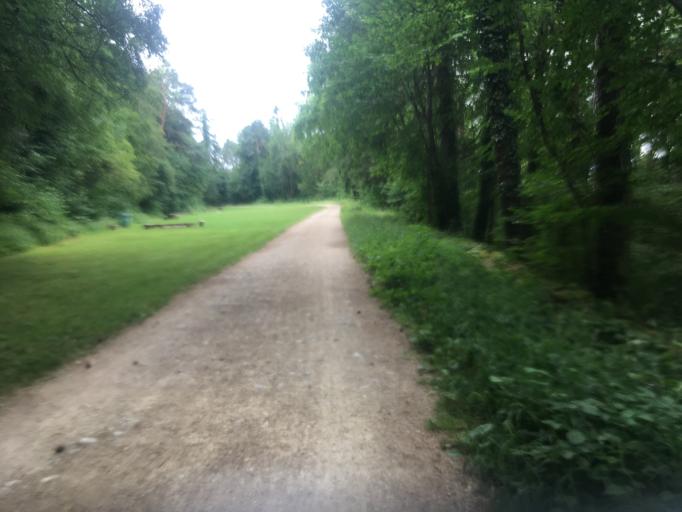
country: CH
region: Bern
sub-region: Jura bernois
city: La Neuveville
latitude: 47.0698
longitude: 7.1389
